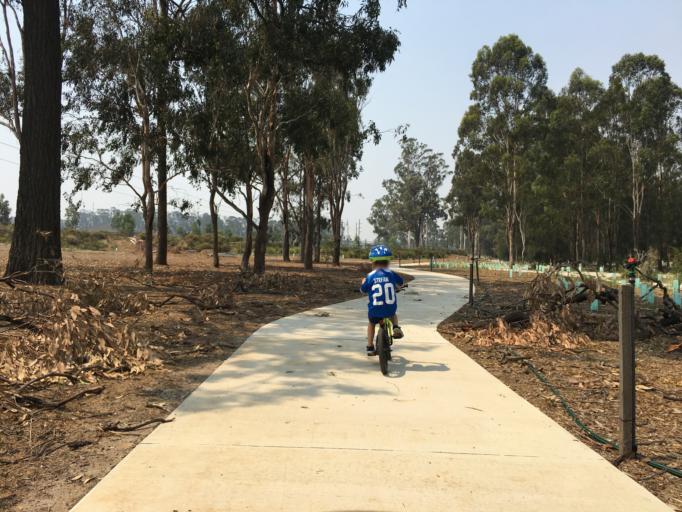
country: AU
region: New South Wales
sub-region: Campbelltown Municipality
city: Denham Court
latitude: -33.9749
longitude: 150.8154
